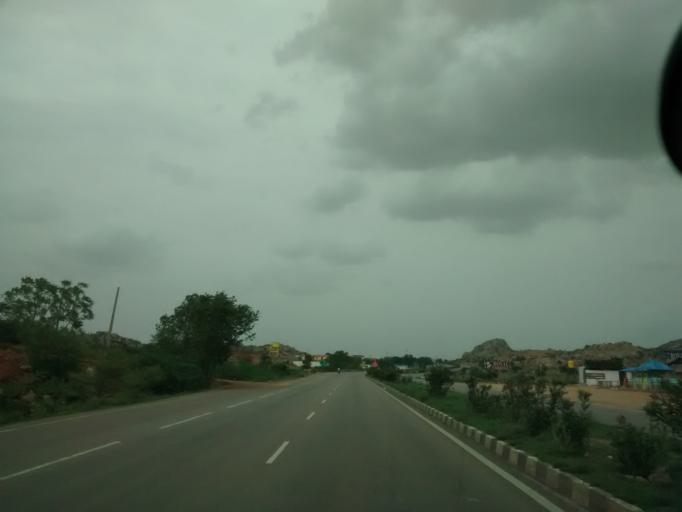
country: IN
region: Andhra Pradesh
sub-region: Kurnool
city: Ramapuram
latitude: 15.1565
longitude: 77.6688
